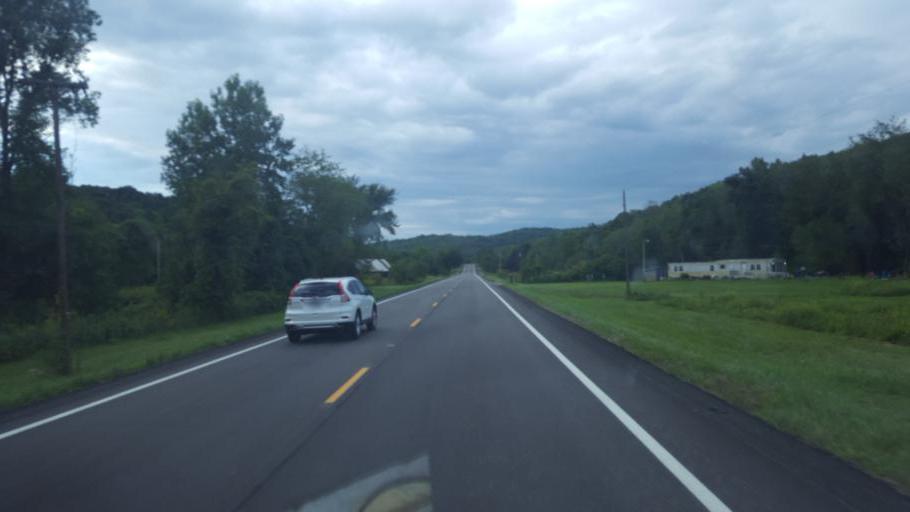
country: US
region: Ohio
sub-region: Knox County
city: Oak Hill
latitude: 40.4621
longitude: -82.1771
